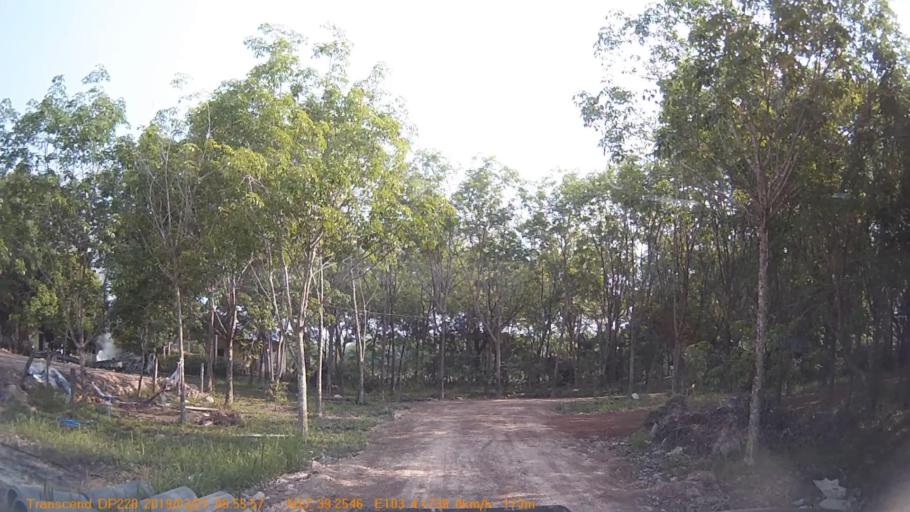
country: TH
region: Changwat Udon Thani
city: Phibun Rak
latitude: 17.6543
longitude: 103.0696
